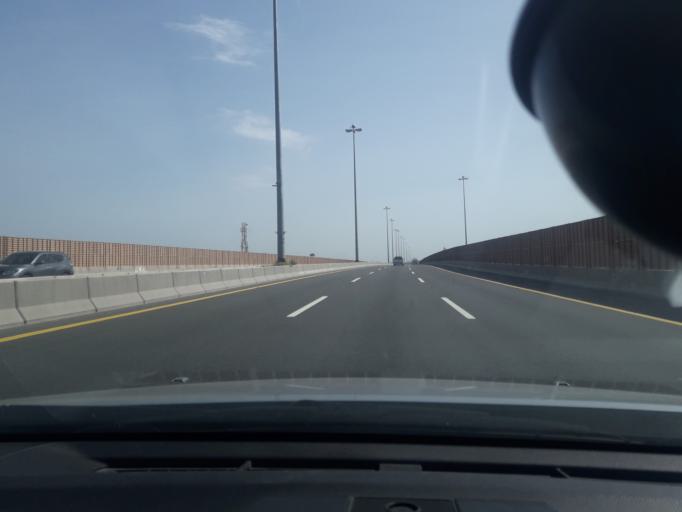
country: SA
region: Al Madinah al Munawwarah
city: Medina
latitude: 24.4442
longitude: 39.6397
